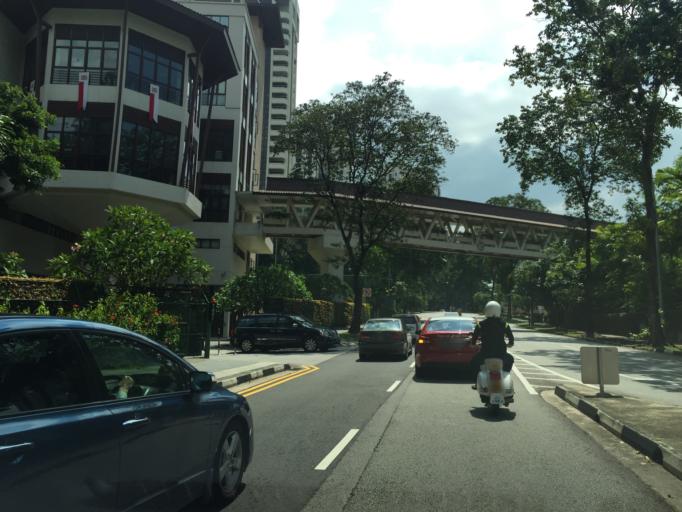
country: SG
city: Singapore
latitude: 1.3092
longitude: 103.8332
